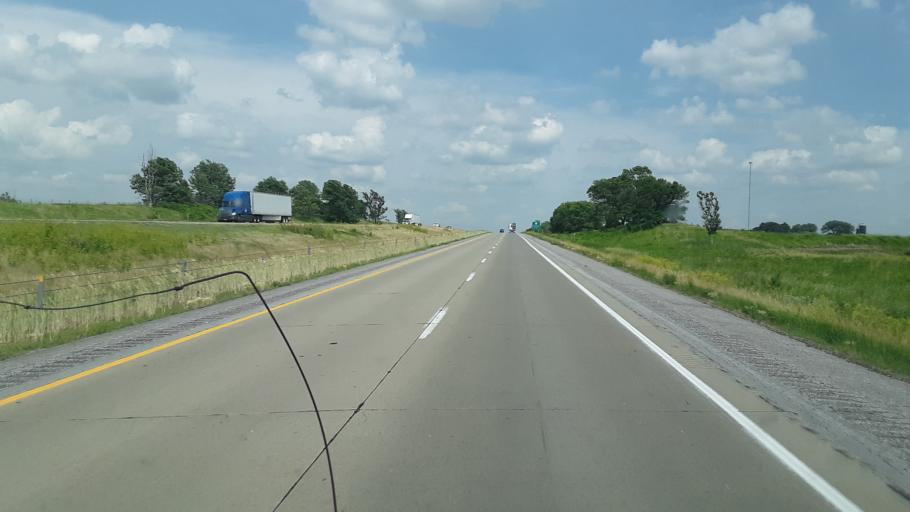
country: US
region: Iowa
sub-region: Cass County
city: Atlantic
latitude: 41.4972
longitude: -94.9744
